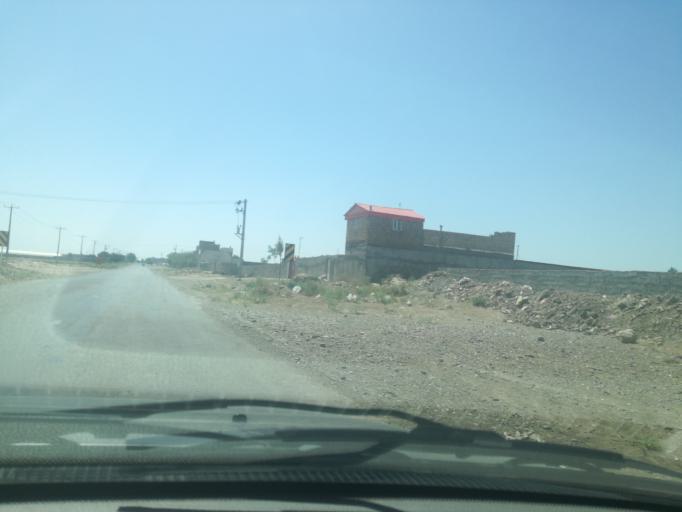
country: IR
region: Razavi Khorasan
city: Sarakhs
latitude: 36.5668
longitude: 61.1410
